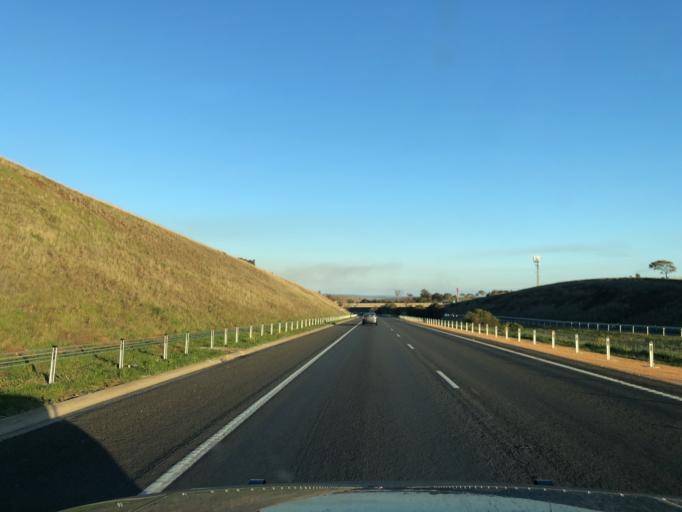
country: AU
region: Victoria
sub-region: Moorabool
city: Bacchus Marsh
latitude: -37.6580
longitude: 144.3730
